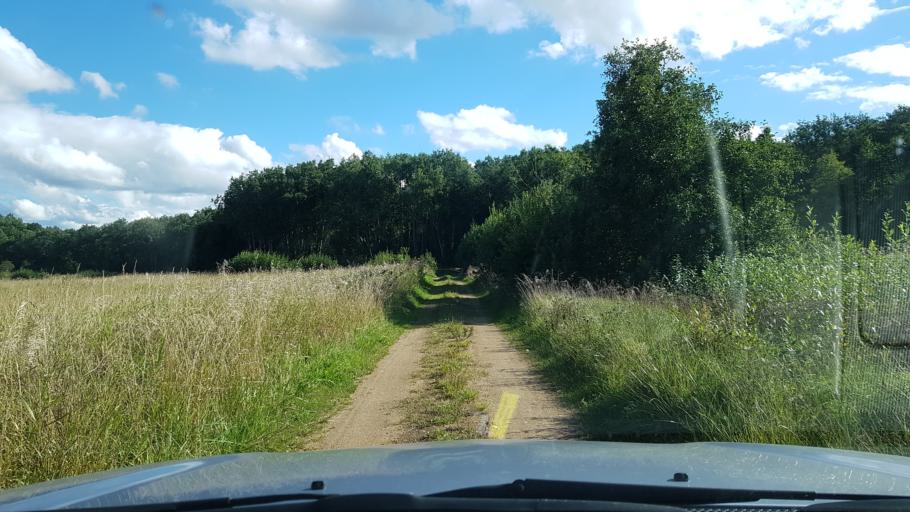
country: EE
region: Harju
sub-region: Rae vald
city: Jueri
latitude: 59.3685
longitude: 24.8391
